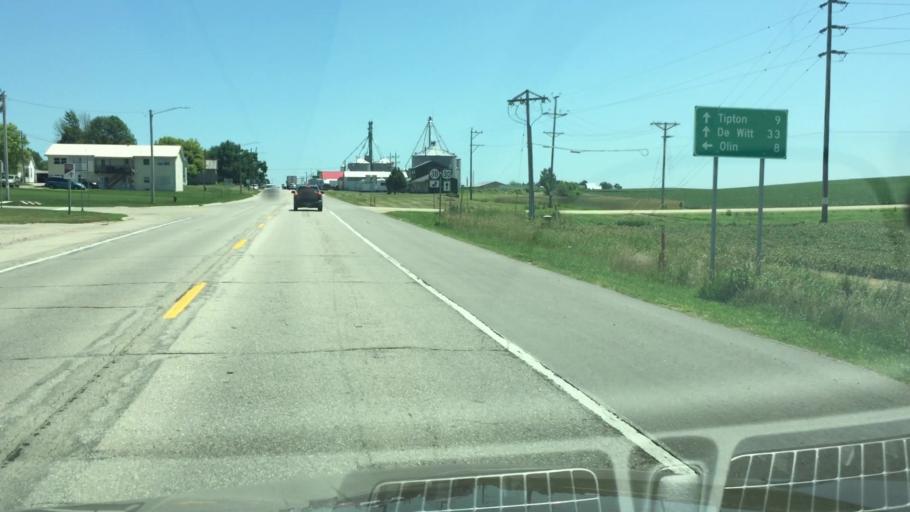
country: US
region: Iowa
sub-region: Cedar County
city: Mechanicsville
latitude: 41.8885
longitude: -91.1528
